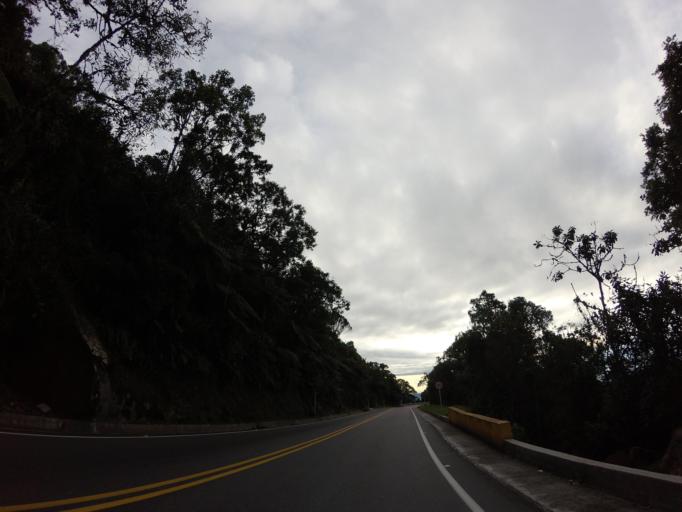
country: CO
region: Tolima
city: Herveo
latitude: 5.0965
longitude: -75.2773
